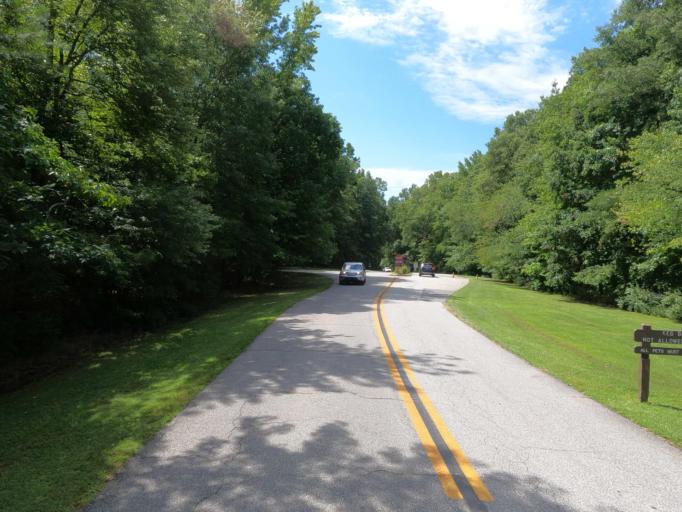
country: US
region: Delaware
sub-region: New Castle County
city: Glasgow
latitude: 39.5668
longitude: -75.7300
